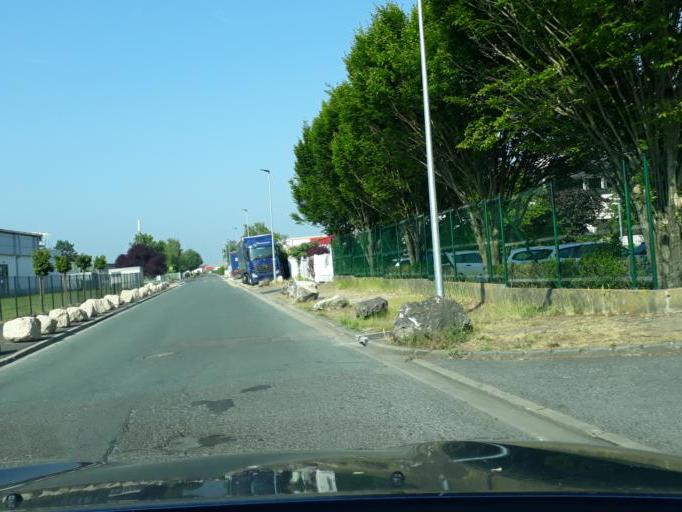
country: FR
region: Centre
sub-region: Departement du Loiret
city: Saint-Jean-de-la-Ruelle
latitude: 47.9026
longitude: 1.8569
